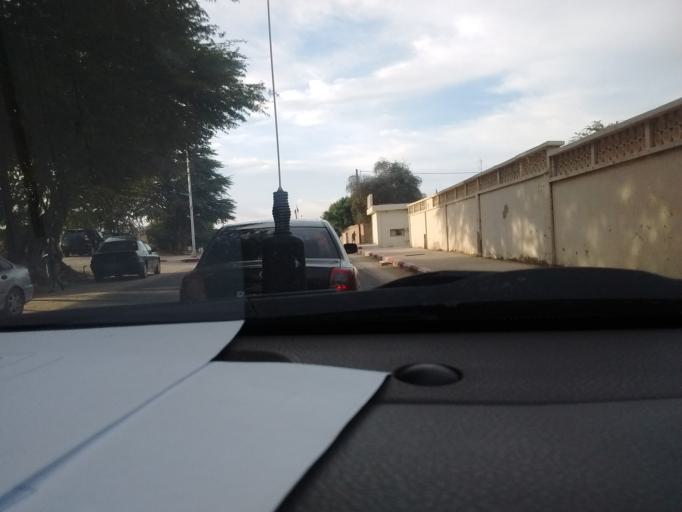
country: MR
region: Nouakchott
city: Nouakchott
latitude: 18.0912
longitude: -15.9835
